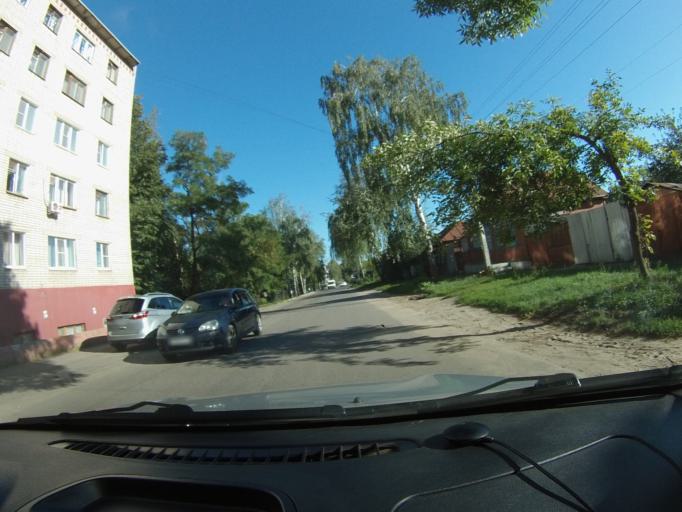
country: RU
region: Tambov
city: Tambov
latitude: 52.7578
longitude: 41.4228
